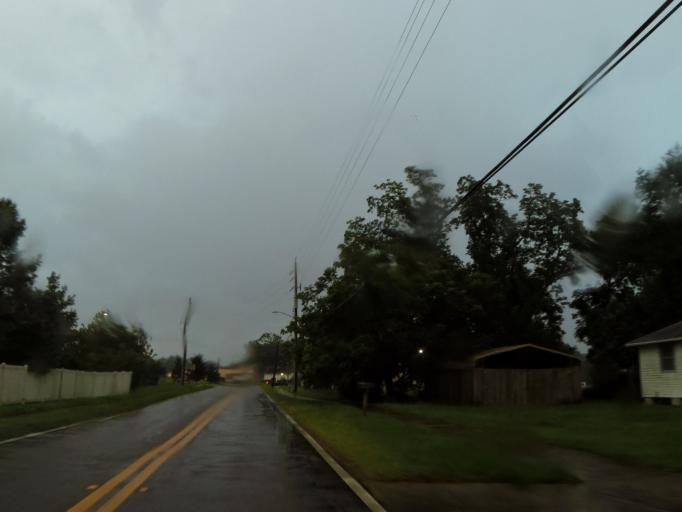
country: US
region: Florida
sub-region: Duval County
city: Jacksonville
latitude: 30.3141
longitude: -81.7349
